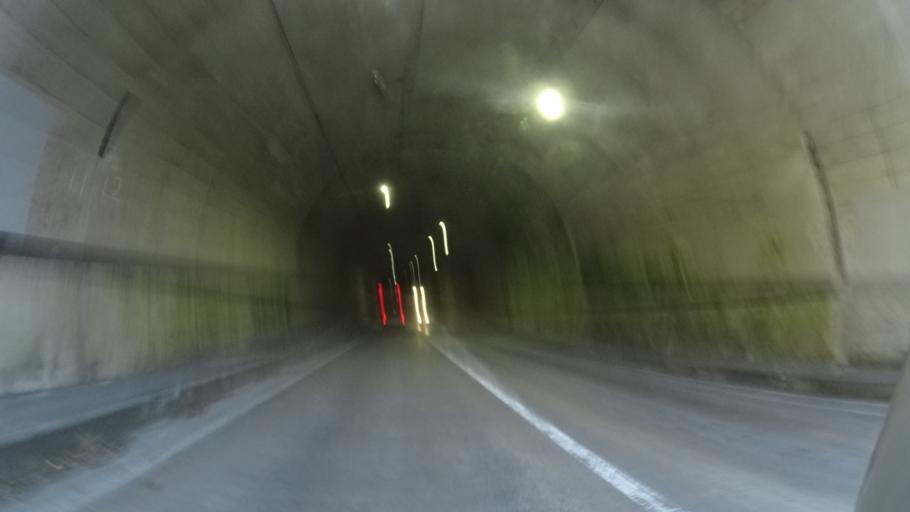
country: JP
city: Asahi
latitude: 35.9575
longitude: 136.0113
